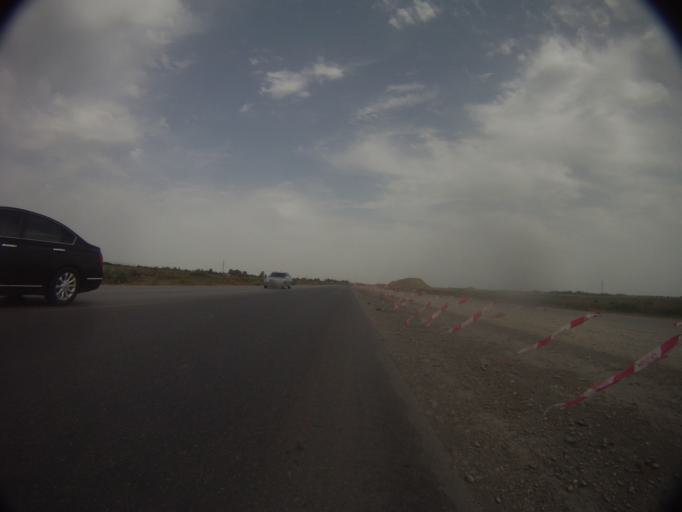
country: AZ
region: Ucar
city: Ujar
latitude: 40.4904
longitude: 47.7666
